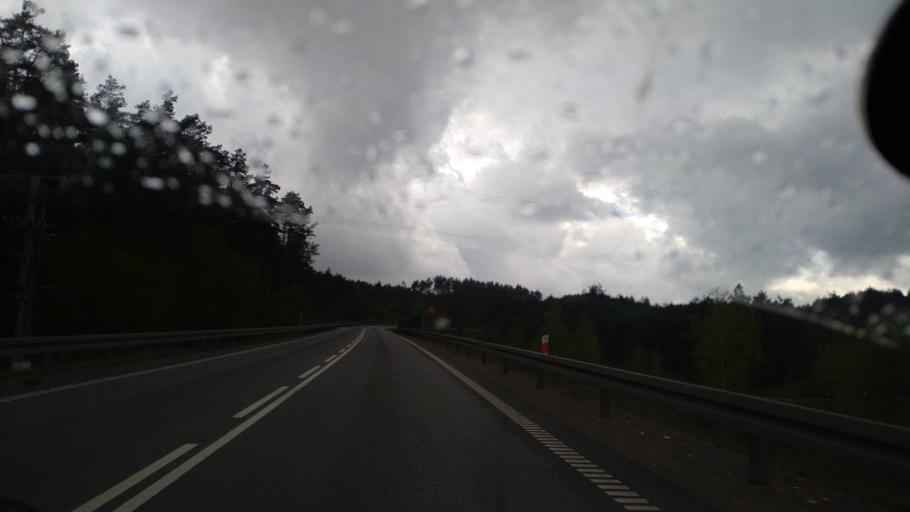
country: PL
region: Pomeranian Voivodeship
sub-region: Powiat tczewski
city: Gniew
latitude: 53.7598
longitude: 18.8114
